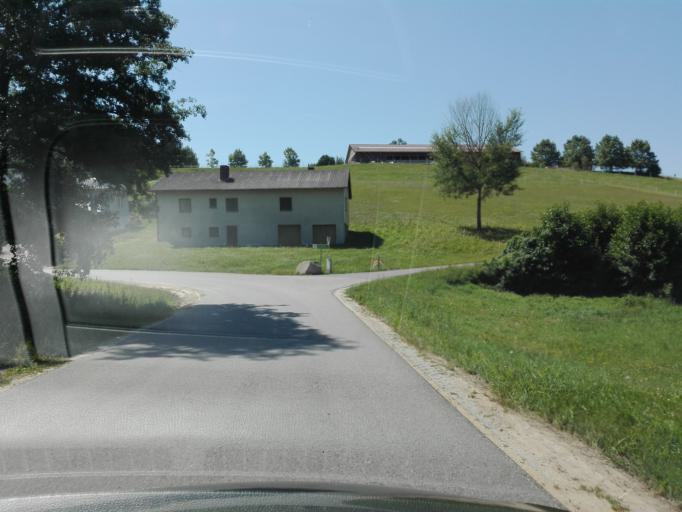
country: AT
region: Upper Austria
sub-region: Politischer Bezirk Urfahr-Umgebung
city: Gallneukirchen
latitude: 48.3290
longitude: 14.3905
